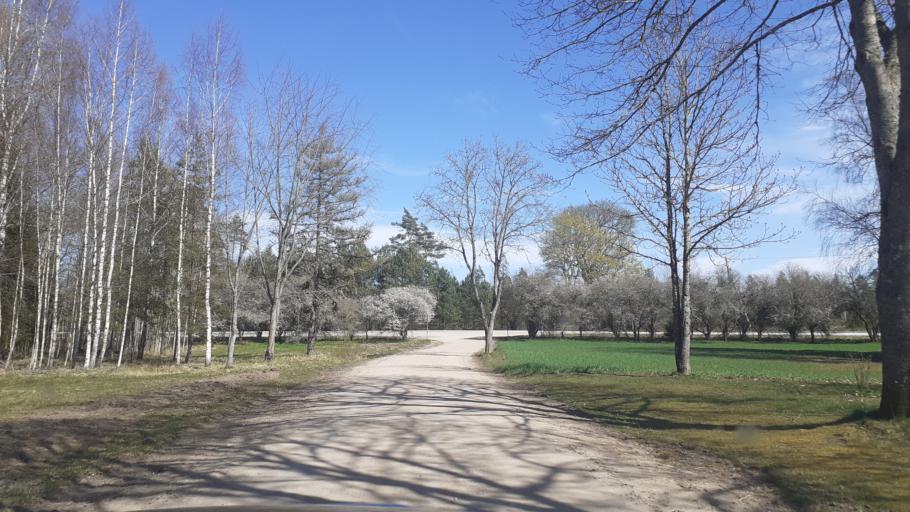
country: LV
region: Kuldigas Rajons
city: Kuldiga
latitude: 56.8535
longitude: 22.0288
